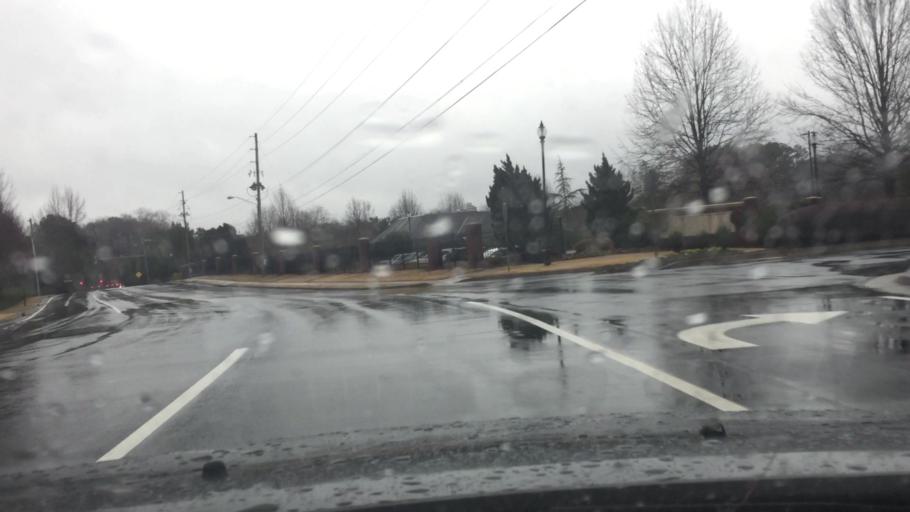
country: US
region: Georgia
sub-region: Cobb County
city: Kennesaw
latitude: 33.9868
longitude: -84.6141
